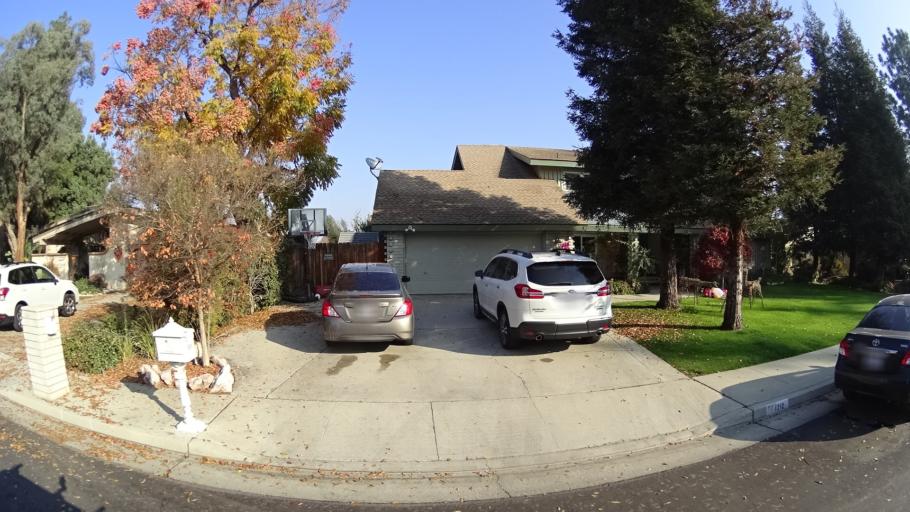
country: US
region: California
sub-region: Kern County
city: Greenacres
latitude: 35.3437
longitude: -119.0723
